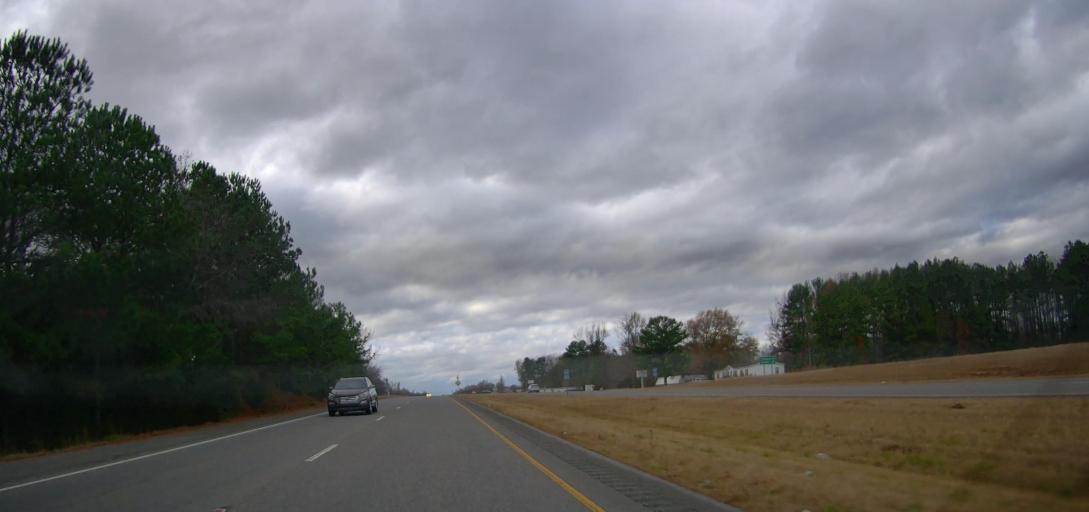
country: US
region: Alabama
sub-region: Lawrence County
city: Town Creek
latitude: 34.5903
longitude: -87.4266
